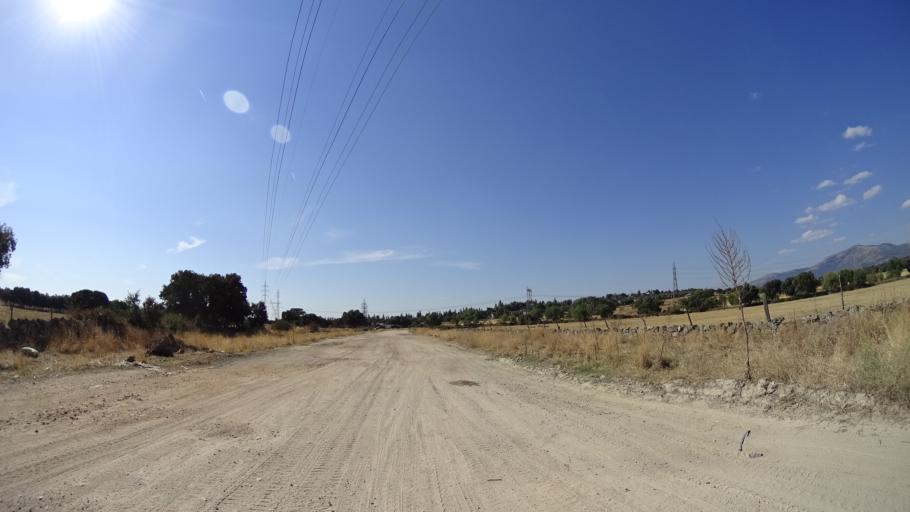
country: ES
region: Madrid
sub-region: Provincia de Madrid
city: Collado-Villalba
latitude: 40.6121
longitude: -4.0209
